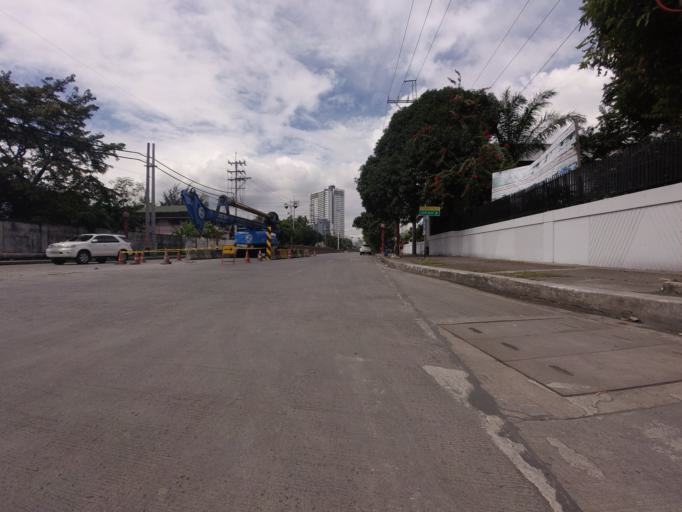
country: PH
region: Metro Manila
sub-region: City of Manila
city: Quiapo
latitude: 14.5812
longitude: 120.9992
